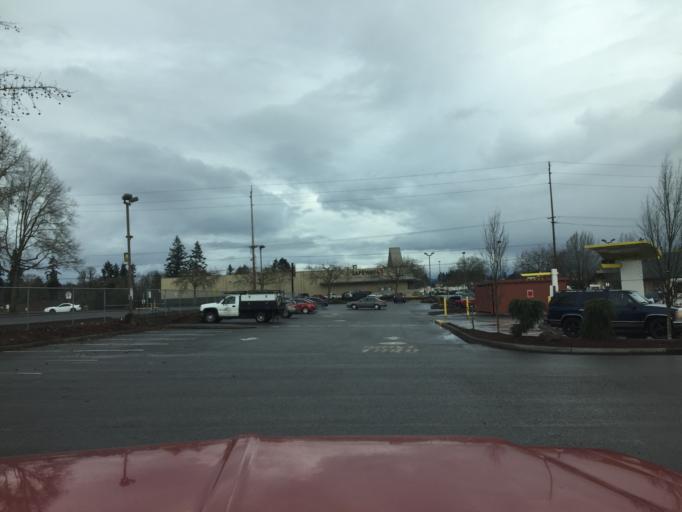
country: US
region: Oregon
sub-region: Columbia County
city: Saint Helens
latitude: 45.8485
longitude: -122.8334
